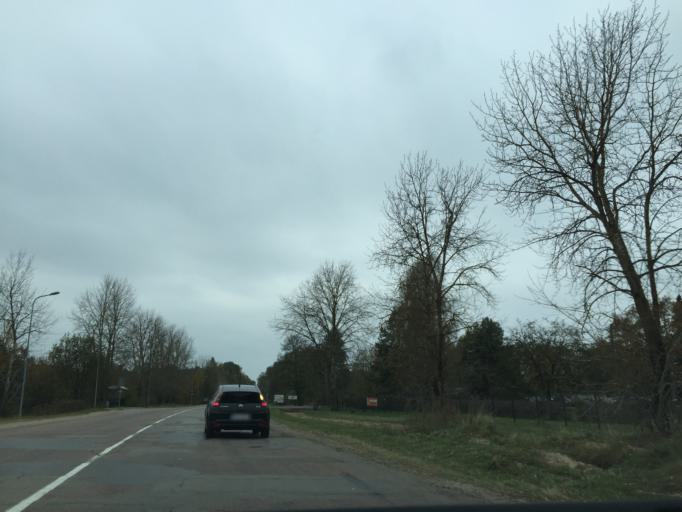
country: LV
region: Marupe
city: Marupe
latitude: 56.8552
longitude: 24.0563
